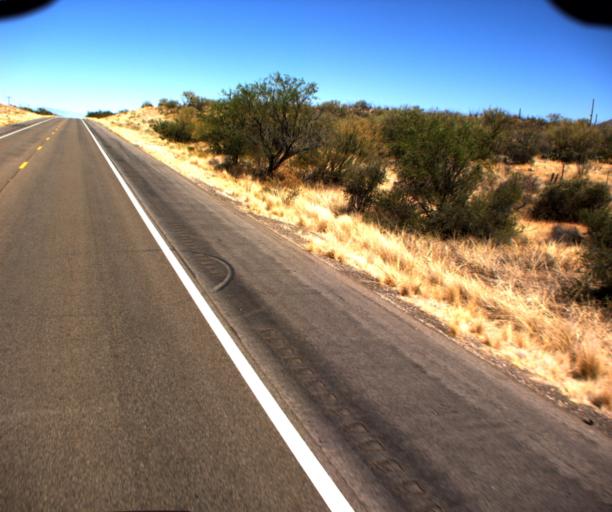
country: US
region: Arizona
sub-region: Pima County
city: Three Points
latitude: 32.0369
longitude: -111.5255
